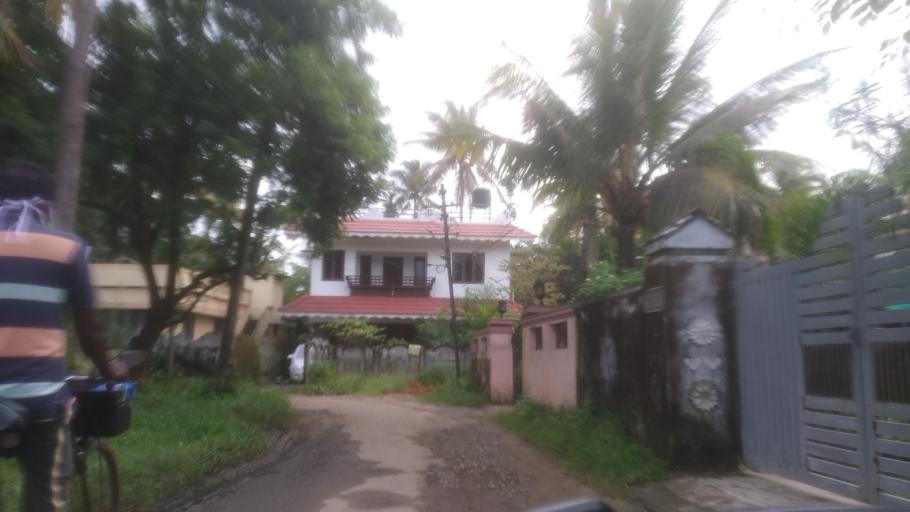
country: IN
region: Kerala
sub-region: Ernakulam
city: Elur
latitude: 10.0944
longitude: 76.2096
